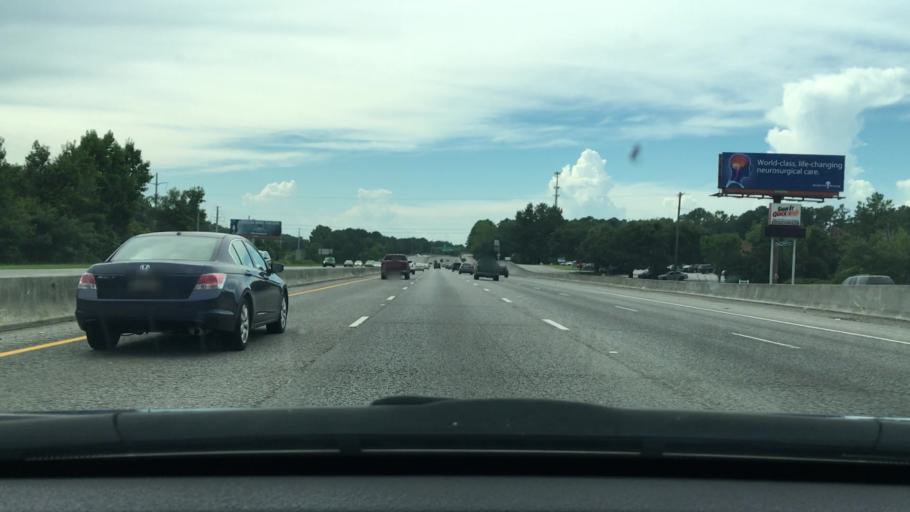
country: US
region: South Carolina
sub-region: Lexington County
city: West Columbia
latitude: 34.0152
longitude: -81.0839
